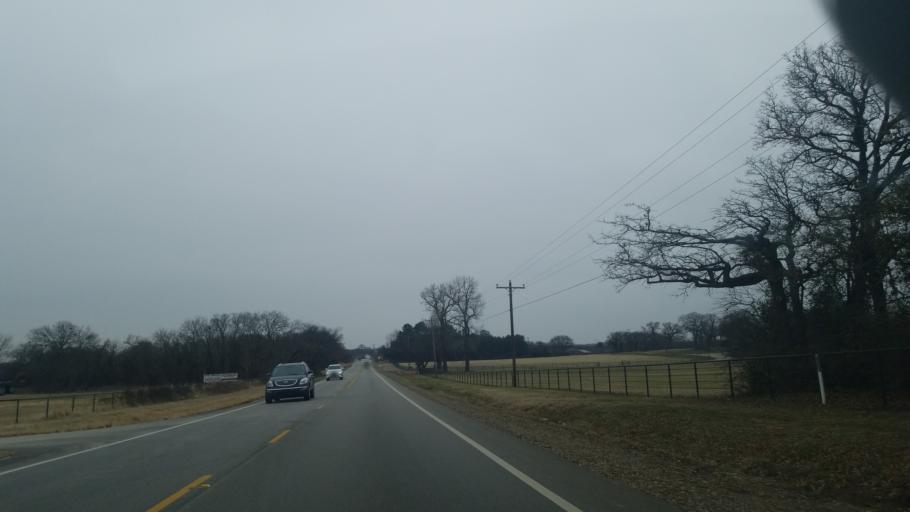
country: US
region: Texas
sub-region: Denton County
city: Bartonville
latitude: 33.1115
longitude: -97.1398
